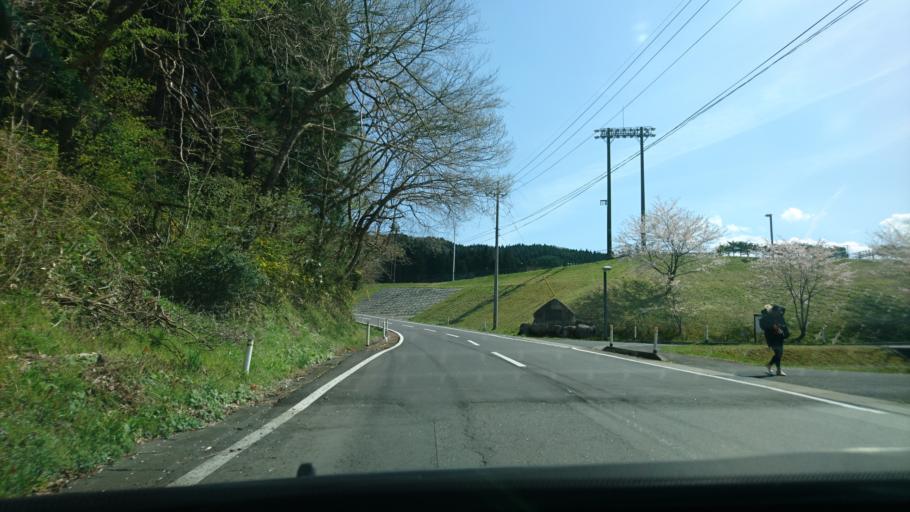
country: JP
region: Iwate
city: Ofunato
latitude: 38.9350
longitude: 141.4496
